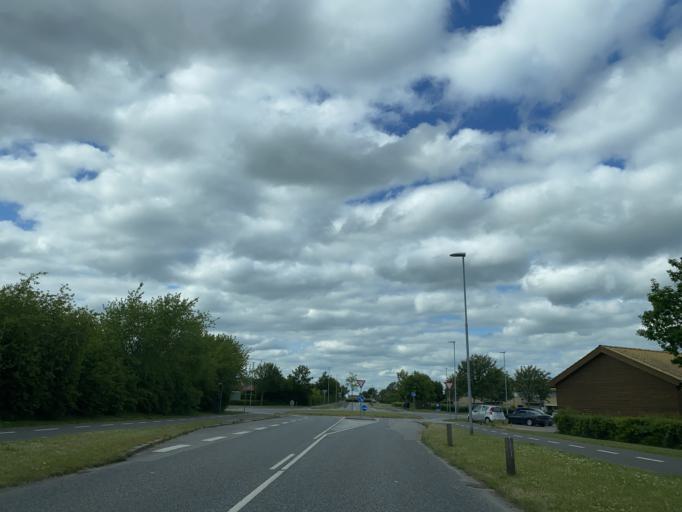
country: DK
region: Central Jutland
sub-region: Arhus Kommune
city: Framlev
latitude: 56.1449
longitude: 9.9874
